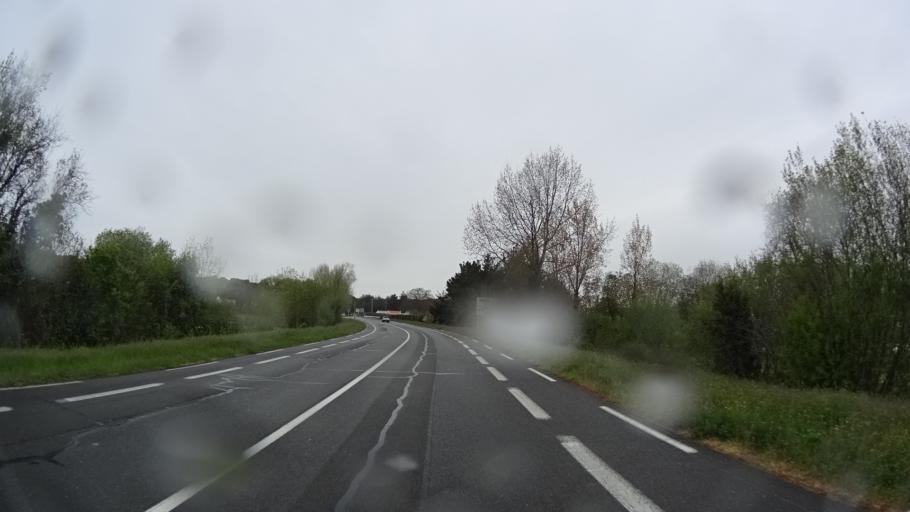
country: FR
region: Pays de la Loire
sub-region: Departement de la Vendee
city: La Barre-de-Monts
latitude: 46.8827
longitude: -2.1219
